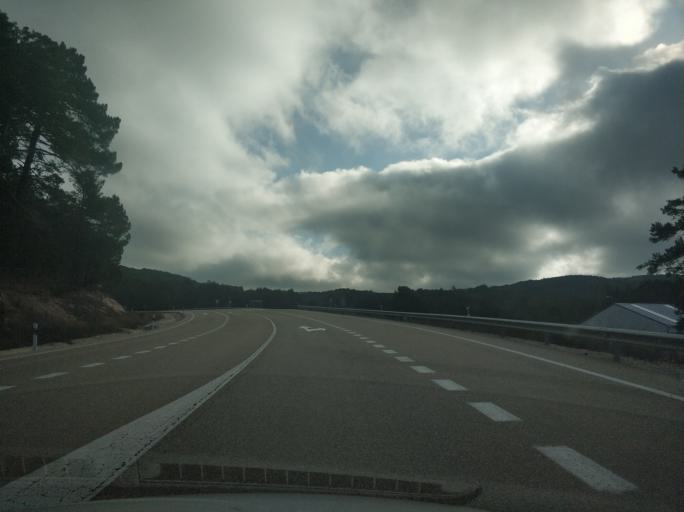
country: ES
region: Castille and Leon
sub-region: Provincia de Soria
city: Navaleno
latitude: 41.8321
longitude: -2.9902
